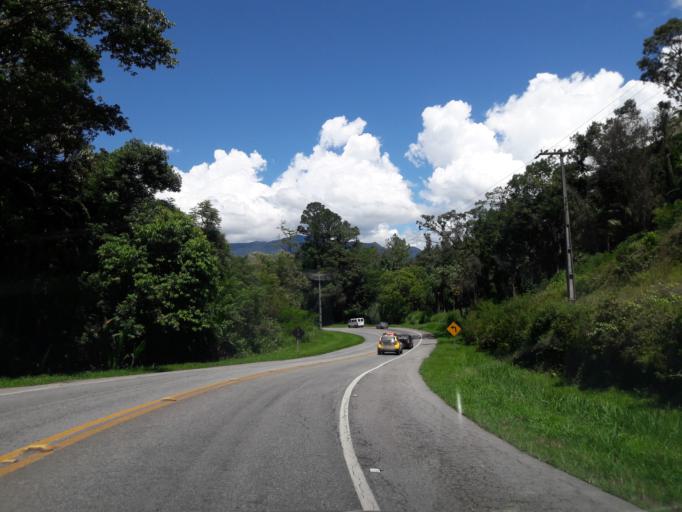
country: BR
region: Parana
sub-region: Antonina
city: Antonina
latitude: -25.5129
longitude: -48.8076
